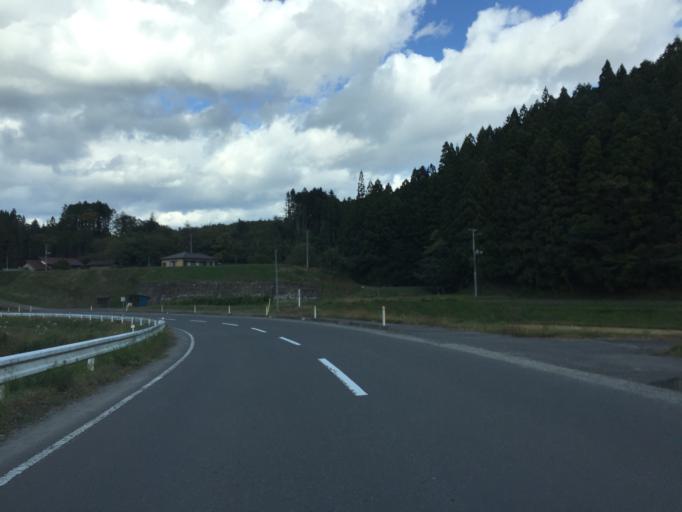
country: JP
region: Miyagi
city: Marumori
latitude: 37.8503
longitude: 140.8318
